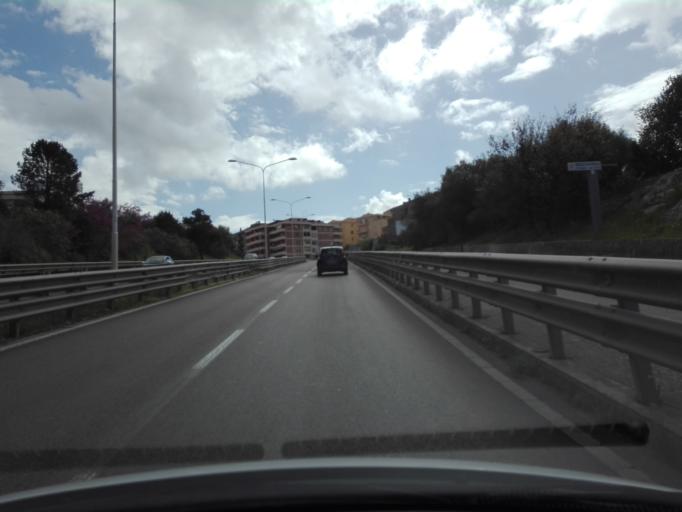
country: IT
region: Sardinia
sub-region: Provincia di Sassari
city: Sassari
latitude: 40.7303
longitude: 8.5765
